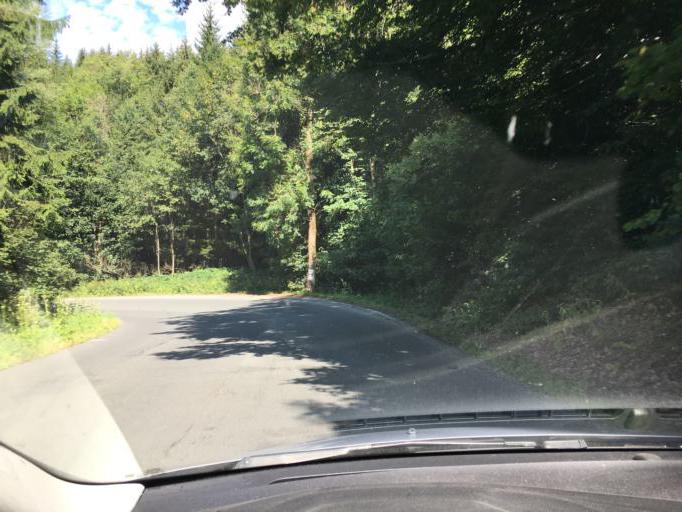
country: CZ
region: Liberecky
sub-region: Okres Semily
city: Vysoke nad Jizerou
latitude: 50.7084
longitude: 15.3737
